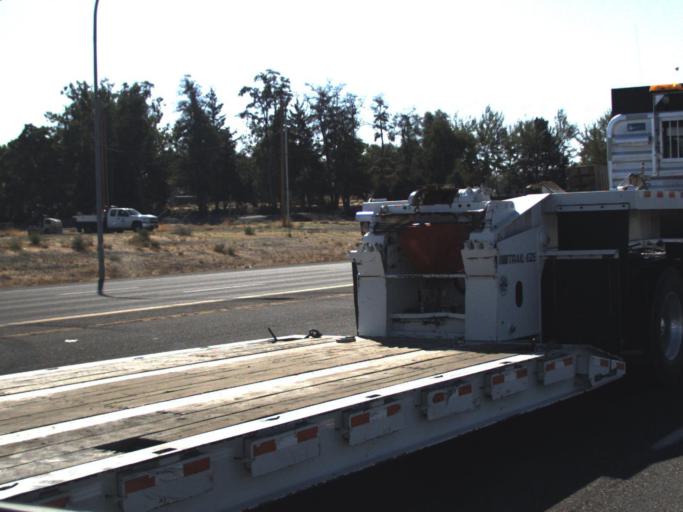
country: US
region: Washington
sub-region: Benton County
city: Richland
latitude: 46.2943
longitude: -119.3040
